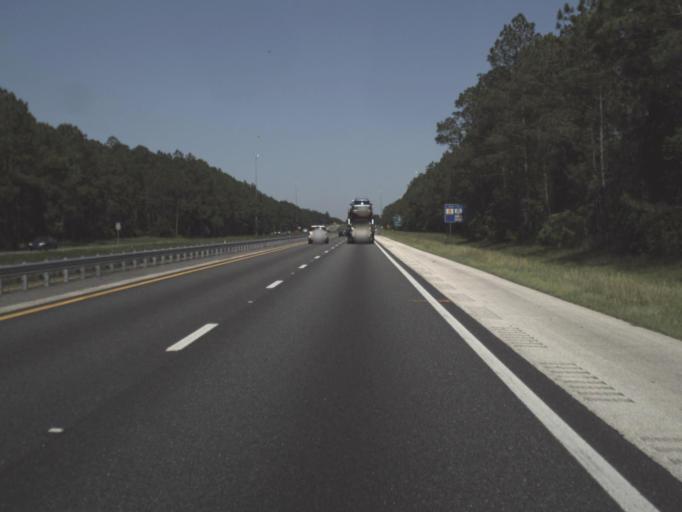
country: US
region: Florida
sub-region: Duval County
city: Baldwin
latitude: 30.2880
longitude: -81.9944
